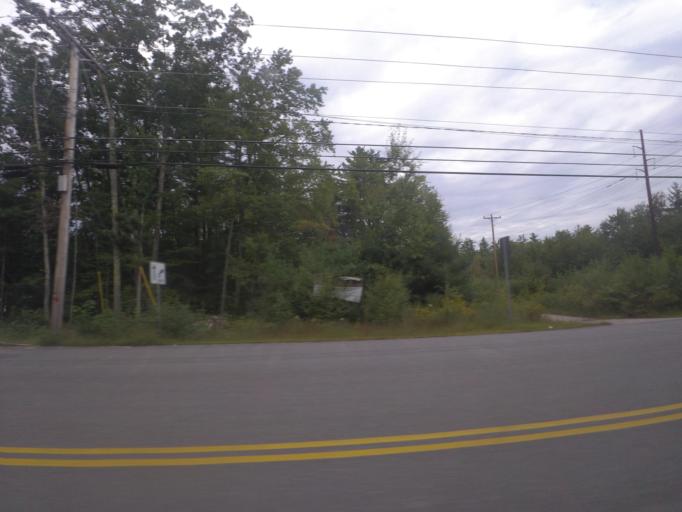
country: US
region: New Hampshire
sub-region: Strafford County
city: Rochester
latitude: 43.2913
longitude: -70.9986
